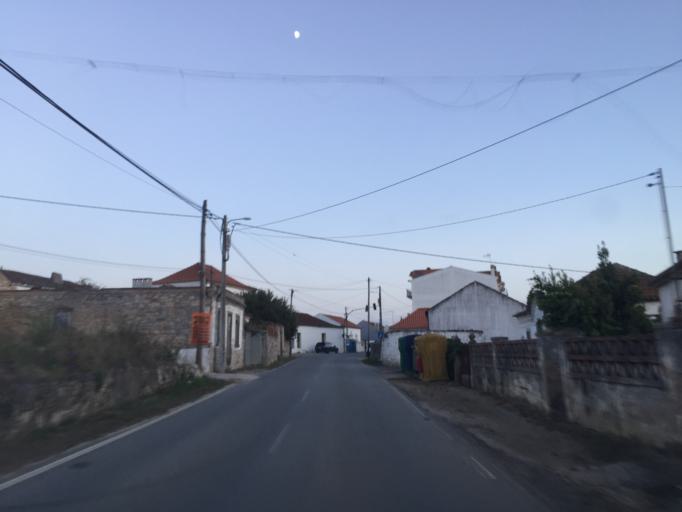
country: PT
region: Leiria
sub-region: Bombarral
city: Bombarral
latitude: 39.2814
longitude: -9.1903
